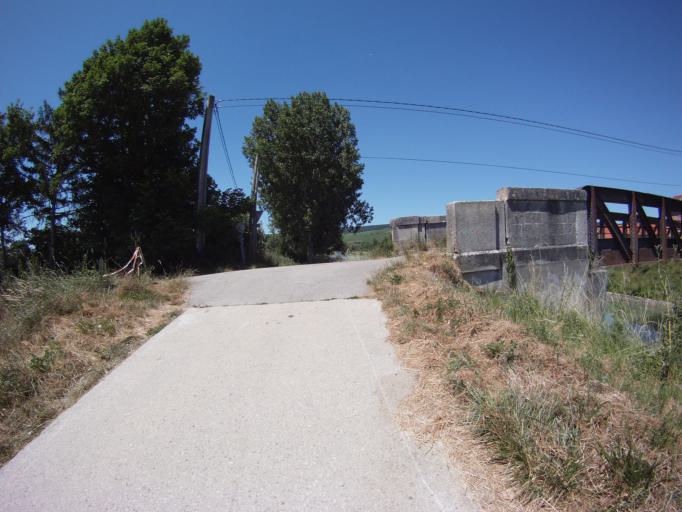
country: FR
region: Champagne-Ardenne
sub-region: Departement de la Marne
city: Epernay
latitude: 49.0669
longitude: 3.9497
